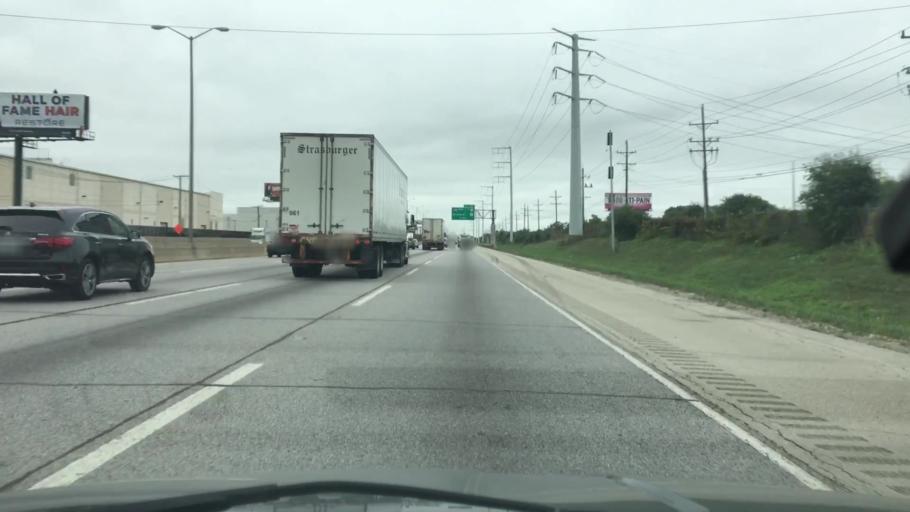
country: US
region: Illinois
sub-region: Cook County
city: Northlake
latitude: 41.9247
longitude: -87.9200
